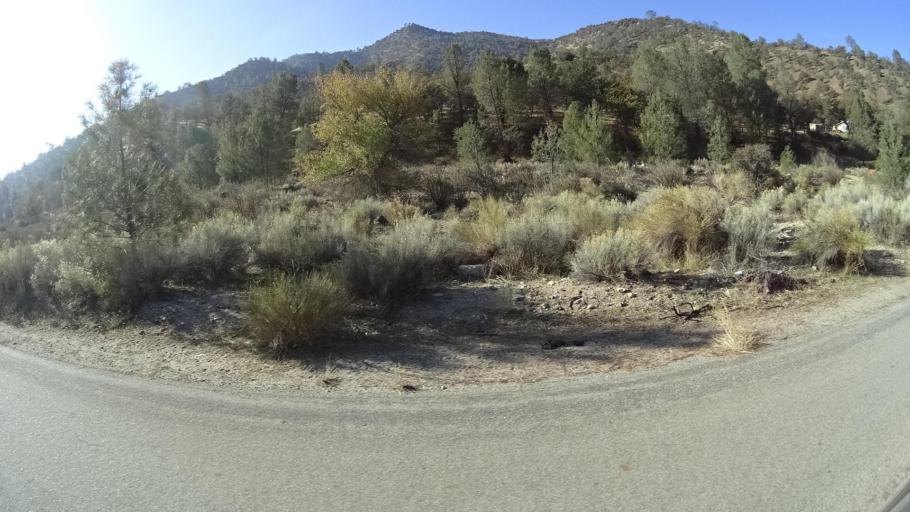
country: US
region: California
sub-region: Kern County
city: Golden Hills
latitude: 35.2996
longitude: -118.4322
